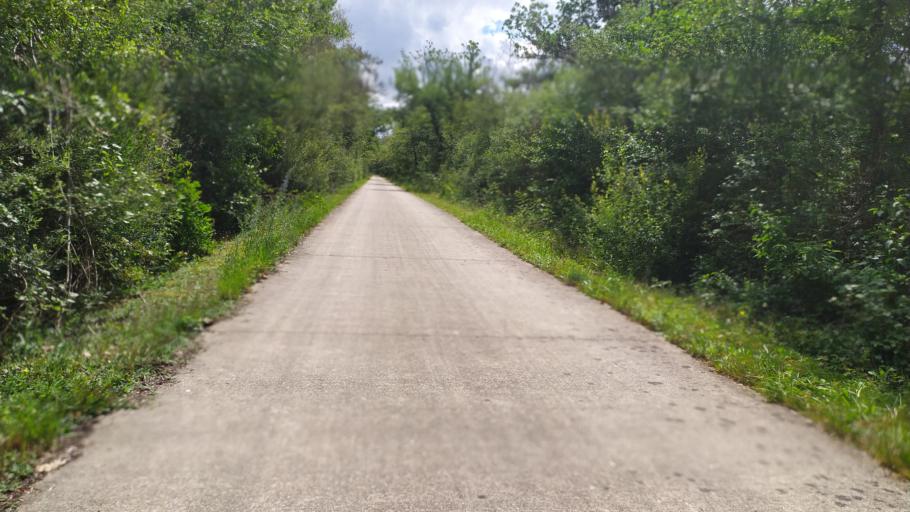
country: BE
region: Wallonia
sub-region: Province du Luxembourg
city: Wellin
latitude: 50.1517
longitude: 5.1337
